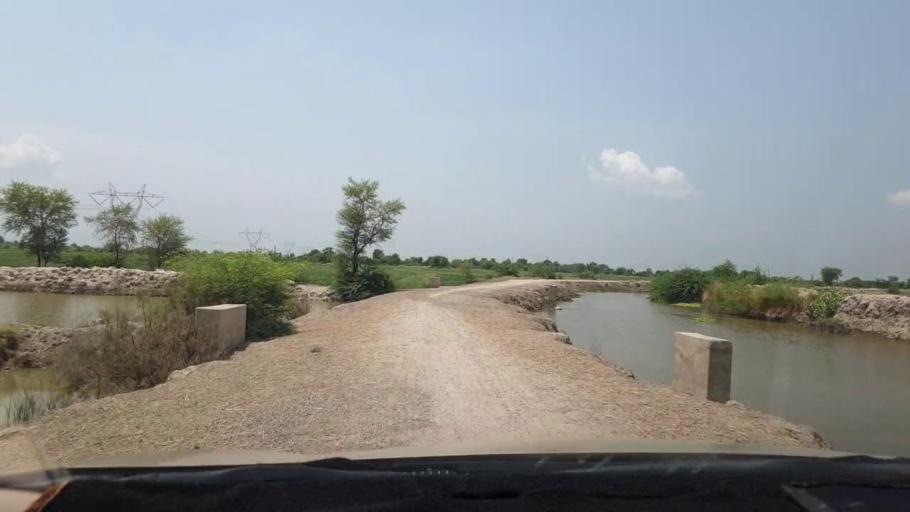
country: PK
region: Sindh
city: Naudero
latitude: 27.6621
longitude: 68.2715
